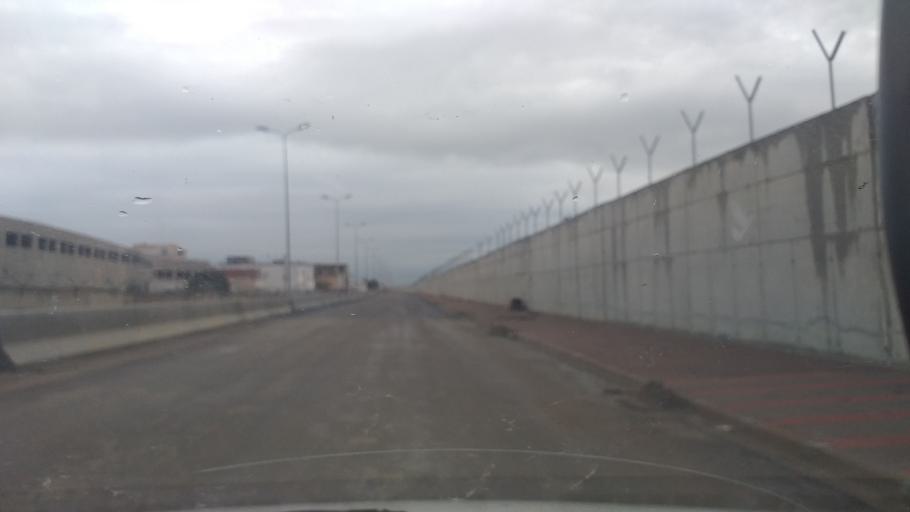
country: TN
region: Ariana
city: Ariana
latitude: 36.8626
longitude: 10.2197
